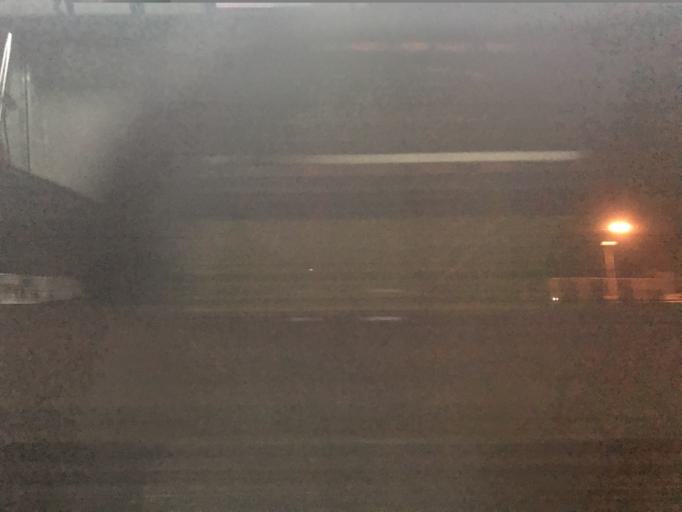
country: TR
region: Istanbul
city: Maltepe
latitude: 40.9086
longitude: 29.1571
